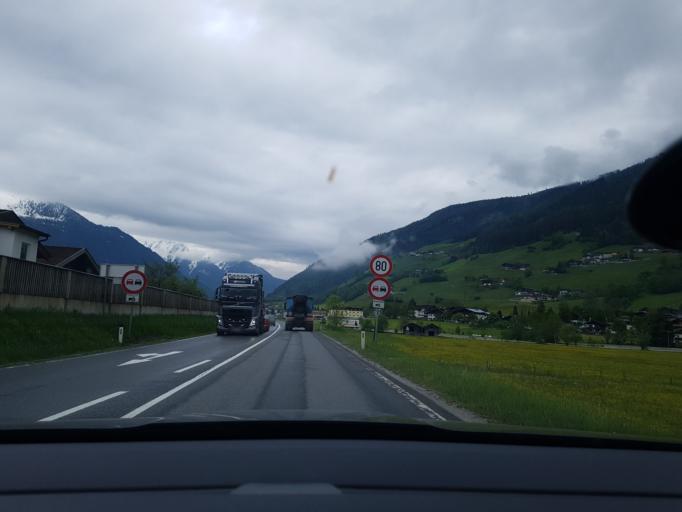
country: AT
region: Salzburg
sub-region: Politischer Bezirk Zell am See
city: Bramberg am Wildkogel
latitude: 47.2703
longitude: 12.3442
